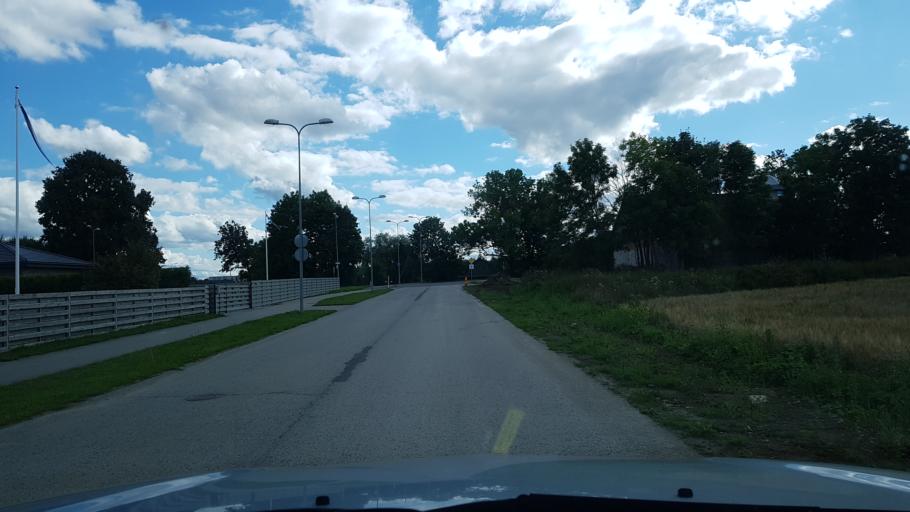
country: EE
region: Harju
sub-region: Rae vald
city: Jueri
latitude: 59.3737
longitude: 24.8324
